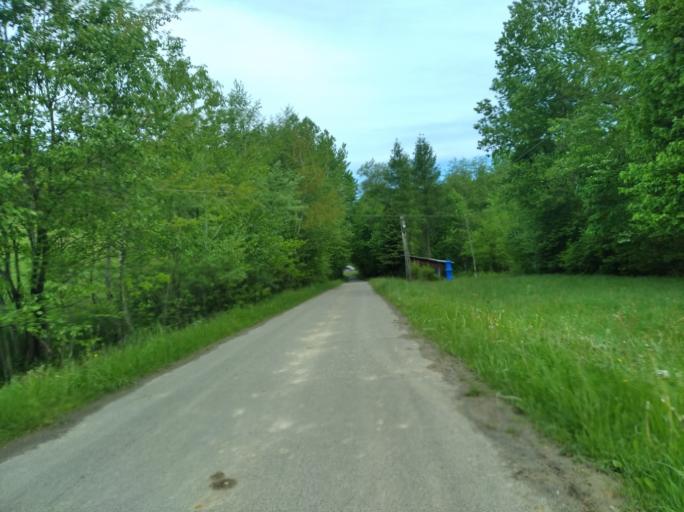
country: PL
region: Subcarpathian Voivodeship
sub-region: Powiat strzyzowski
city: Strzyzow
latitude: 49.9170
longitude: 21.7573
